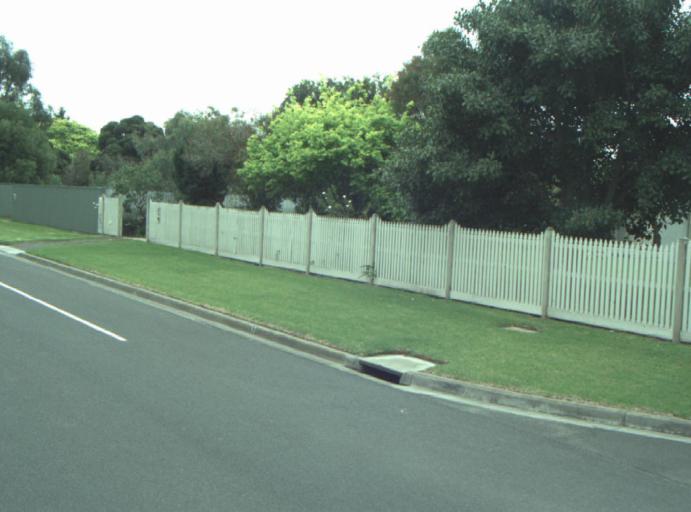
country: AU
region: Victoria
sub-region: Greater Geelong
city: East Geelong
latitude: -38.1652
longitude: 144.4041
